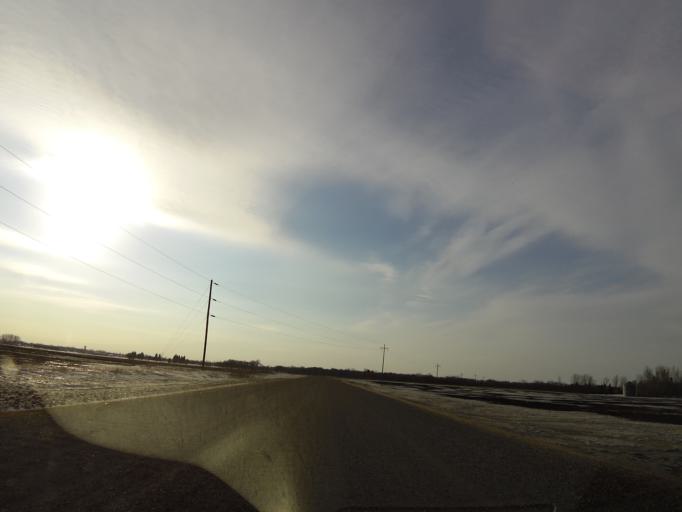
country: US
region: North Dakota
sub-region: Walsh County
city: Grafton
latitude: 48.4197
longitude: -97.3733
